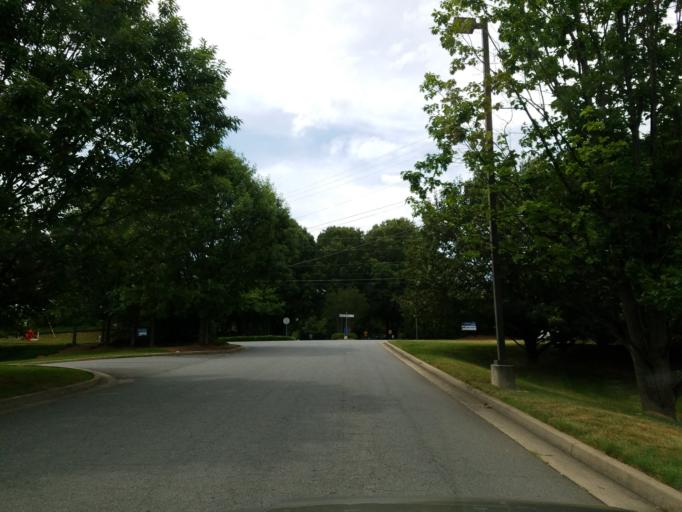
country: US
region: Georgia
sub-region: Cobb County
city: Smyrna
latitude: 33.9166
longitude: -84.4949
